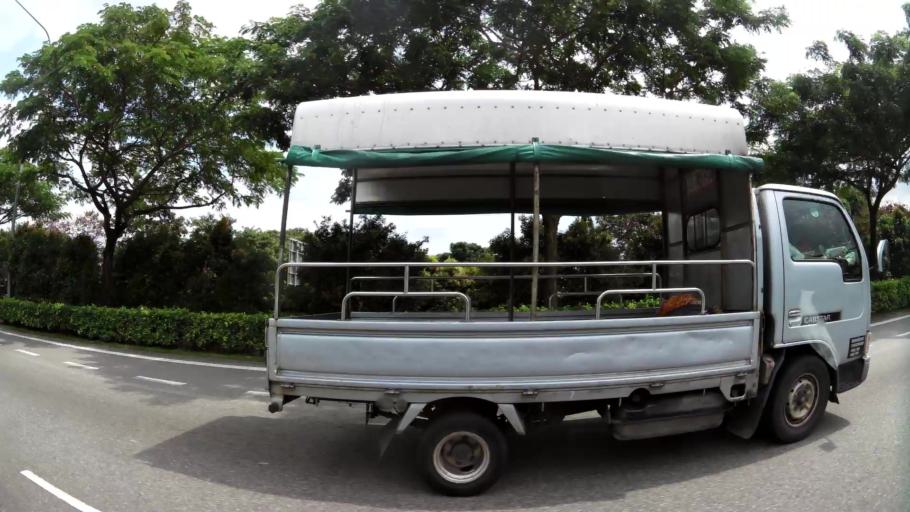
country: SG
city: Singapore
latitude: 1.3713
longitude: 103.8606
